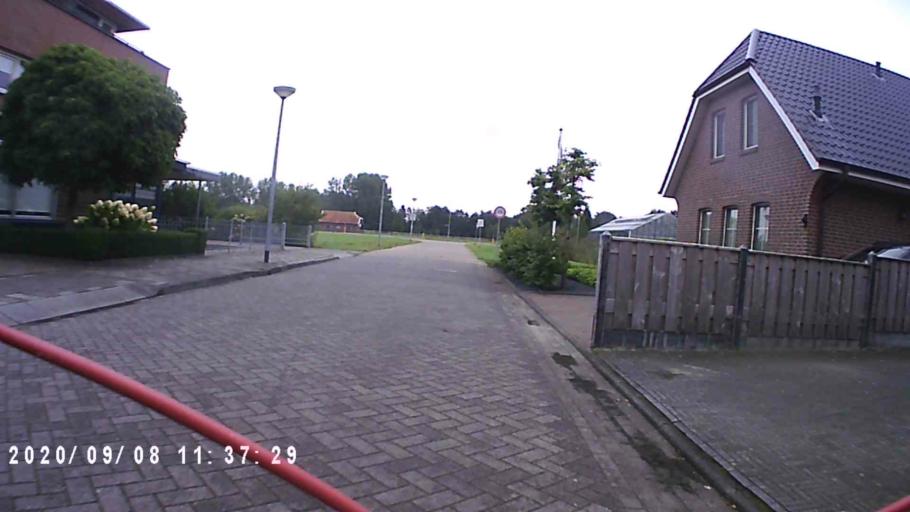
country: NL
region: Groningen
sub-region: Gemeente Hoogezand-Sappemeer
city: Sappemeer
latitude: 53.1552
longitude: 6.7812
